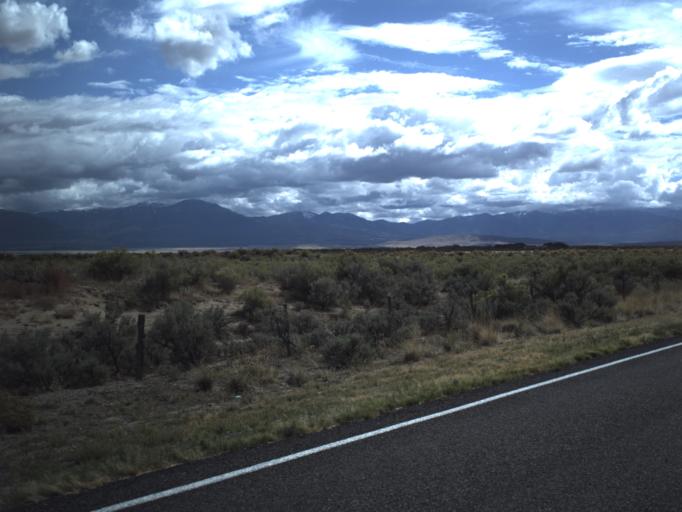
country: US
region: Utah
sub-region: Millard County
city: Fillmore
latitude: 39.1490
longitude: -112.4099
